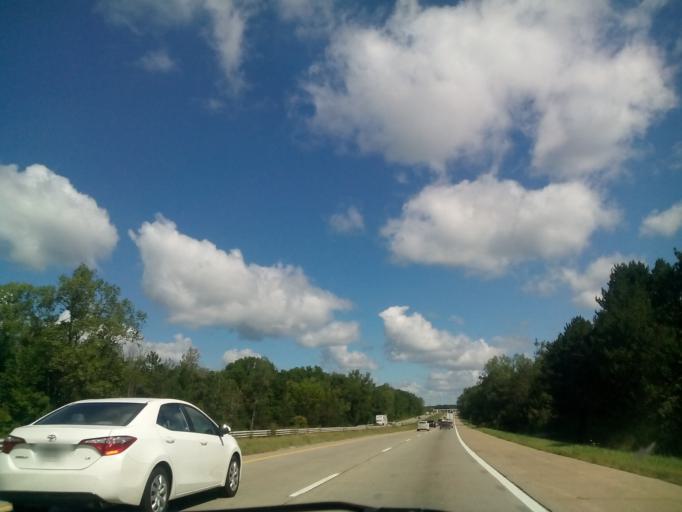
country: US
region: Michigan
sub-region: Genesee County
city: Lake Fenton
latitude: 42.8497
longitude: -83.7395
